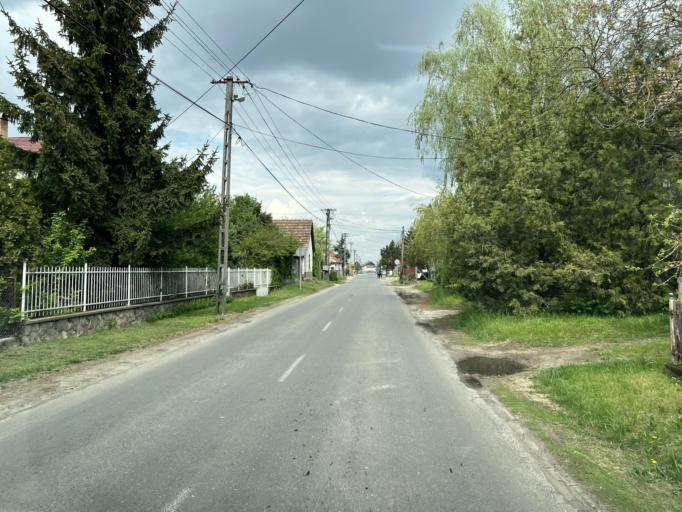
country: HU
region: Pest
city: Hernad
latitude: 47.1595
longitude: 19.3978
